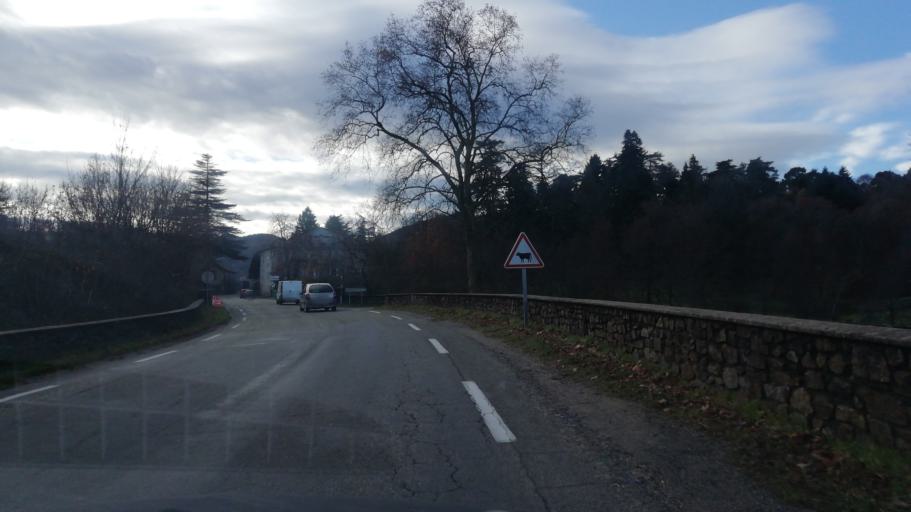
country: FR
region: Languedoc-Roussillon
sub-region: Departement du Gard
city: Lasalle
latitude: 44.0379
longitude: 3.8612
